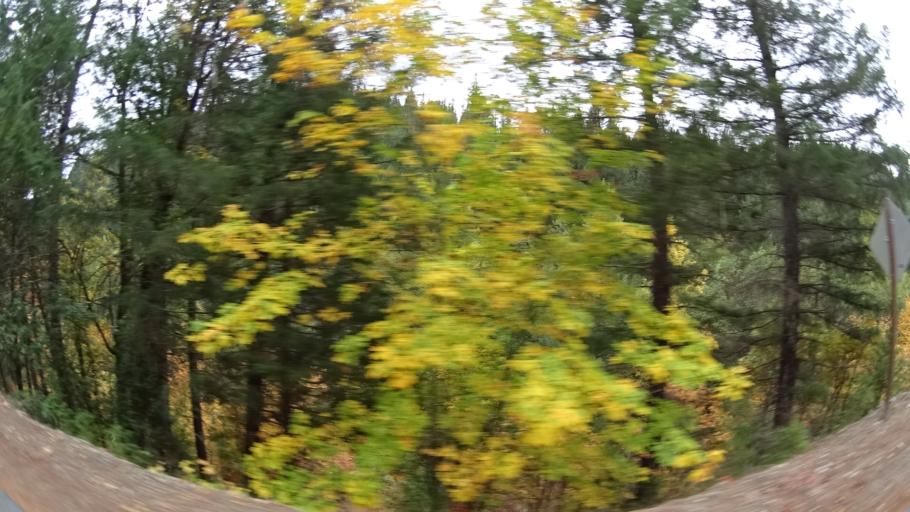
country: US
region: California
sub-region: Siskiyou County
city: Happy Camp
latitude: 41.9102
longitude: -123.4487
